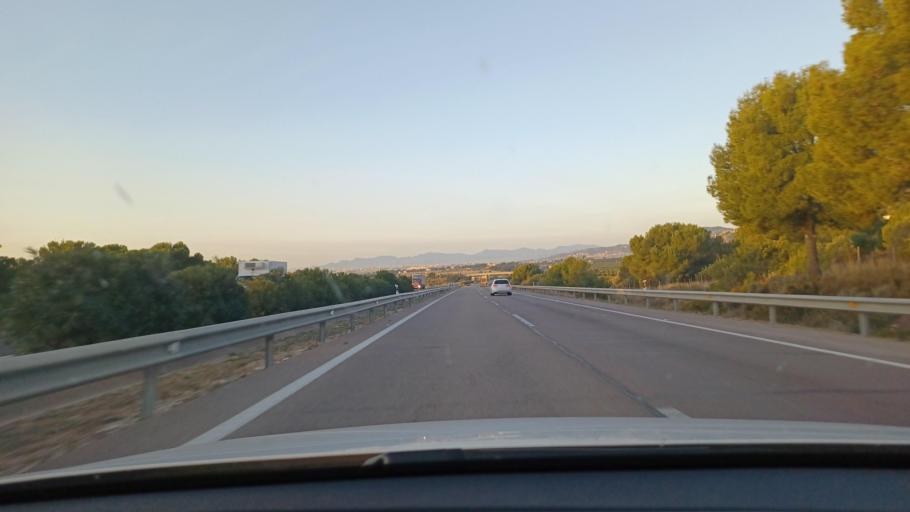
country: ES
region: Valencia
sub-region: Provincia de Castello
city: Benicassim
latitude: 40.0390
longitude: 0.0181
